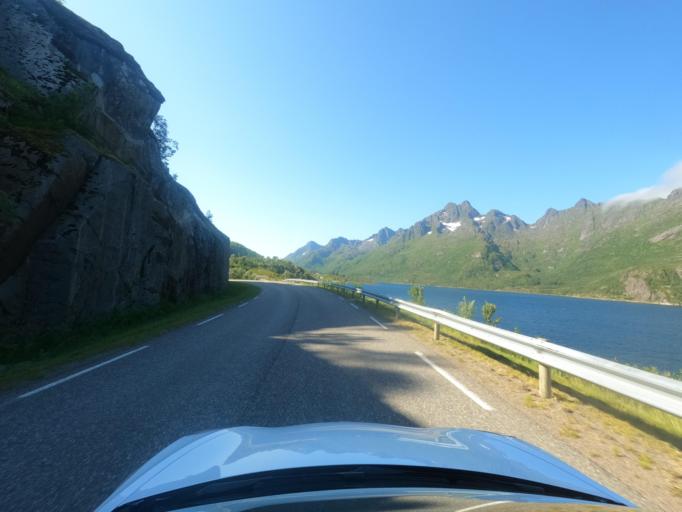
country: NO
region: Nordland
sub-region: Hadsel
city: Stokmarknes
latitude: 68.4395
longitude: 15.1867
